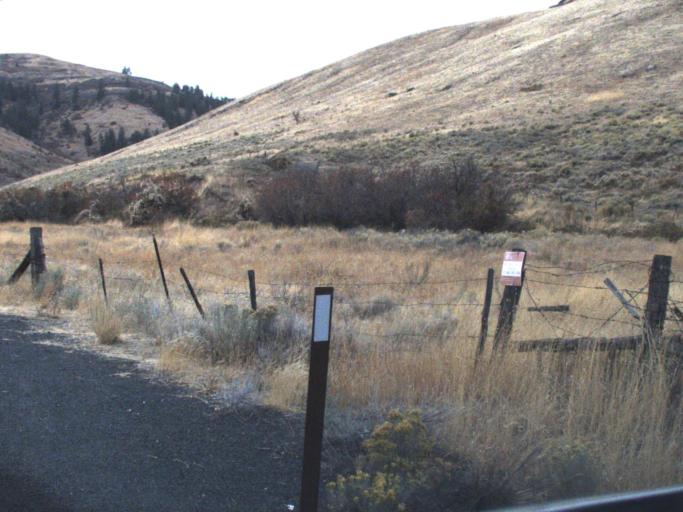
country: US
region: Washington
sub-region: Okanogan County
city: Coulee Dam
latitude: 47.8827
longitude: -118.7184
